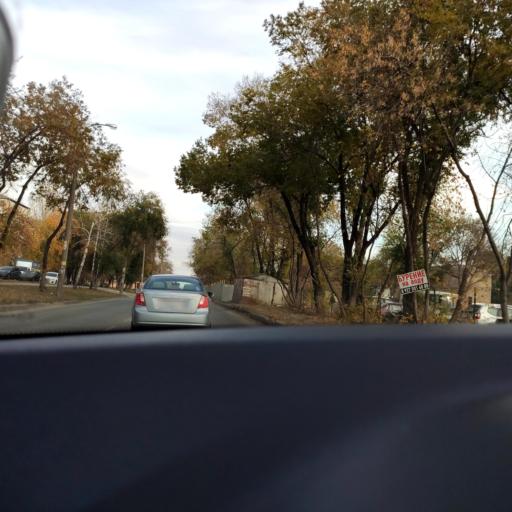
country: RU
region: Samara
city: Samara
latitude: 53.1872
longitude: 50.1850
